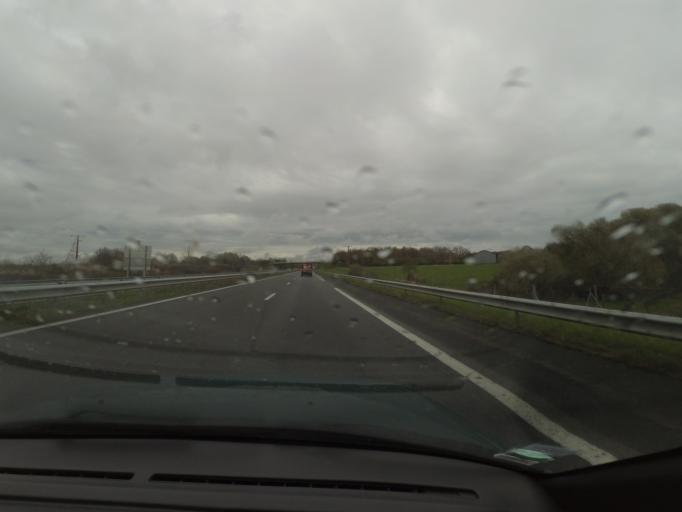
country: FR
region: Pays de la Loire
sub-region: Departement de la Sarthe
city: Parce-sur-Sarthe
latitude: 47.8127
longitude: -0.1612
